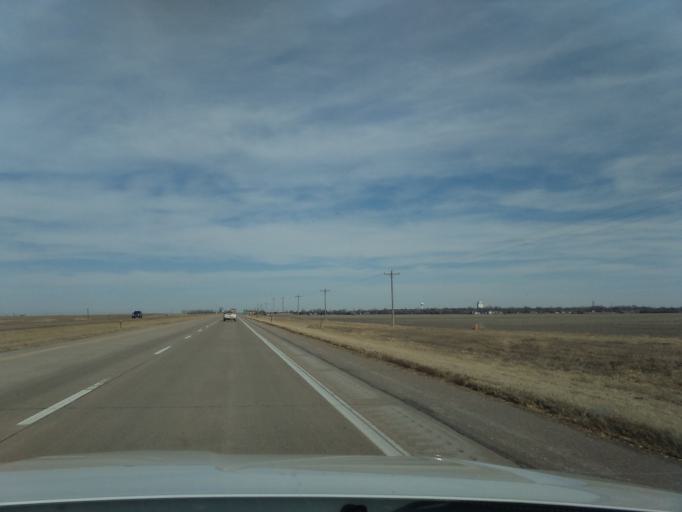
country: US
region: Nebraska
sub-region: Fillmore County
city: Geneva
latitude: 40.6143
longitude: -97.5956
